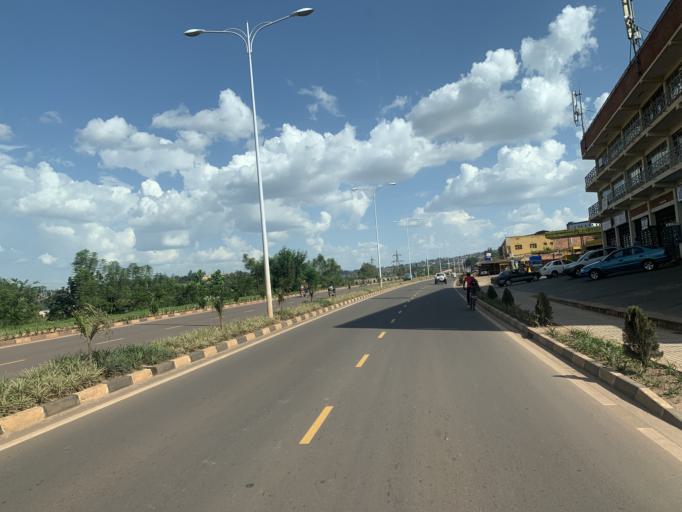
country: RW
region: Kigali
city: Kigali
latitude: -1.9659
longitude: 30.0812
